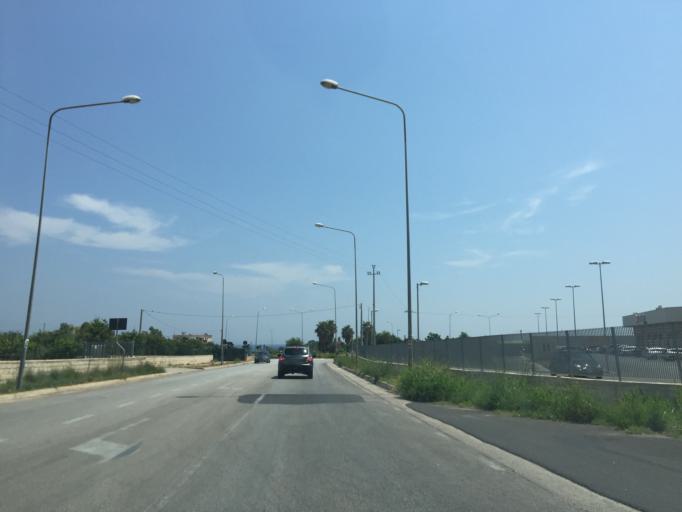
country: IT
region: Sicily
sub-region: Provincia di Siracusa
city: Avola
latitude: 36.9204
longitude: 15.1455
